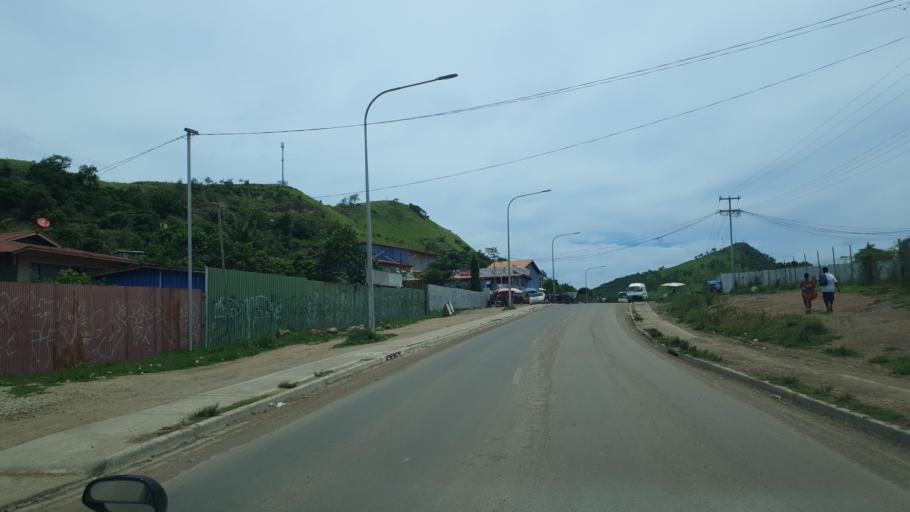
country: PG
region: National Capital
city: Port Moresby
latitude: -9.5197
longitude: 147.2409
